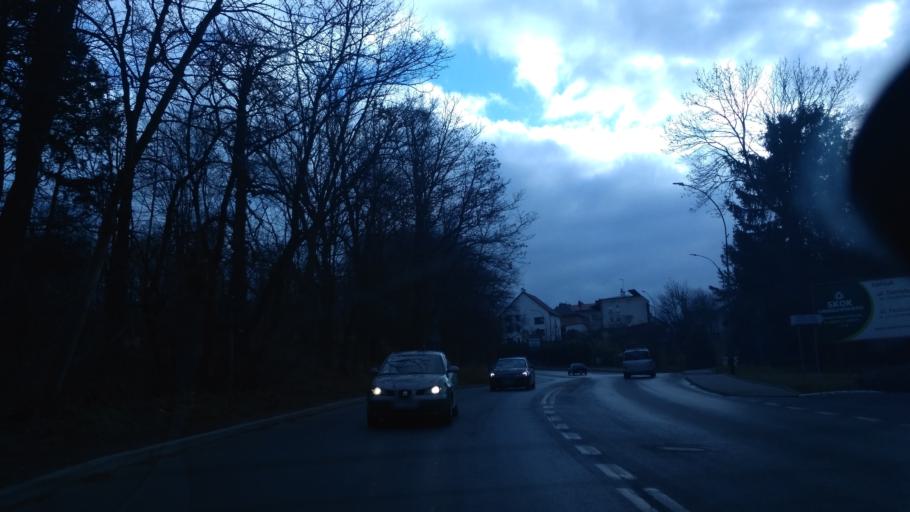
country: PL
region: Subcarpathian Voivodeship
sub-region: Powiat lancucki
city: Lancut
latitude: 50.0782
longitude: 22.2343
